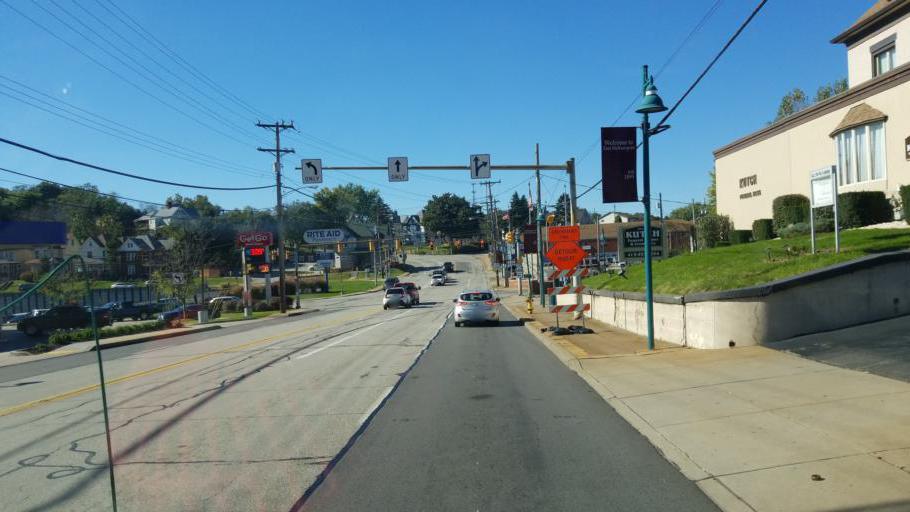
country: US
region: Pennsylvania
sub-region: Allegheny County
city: North Versailles
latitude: 40.3809
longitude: -79.8110
